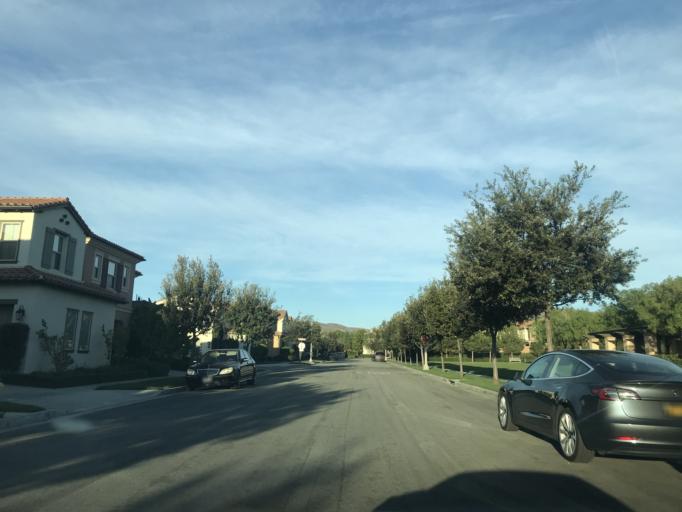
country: US
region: California
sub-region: Orange County
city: North Tustin
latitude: 33.7074
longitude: -117.7424
